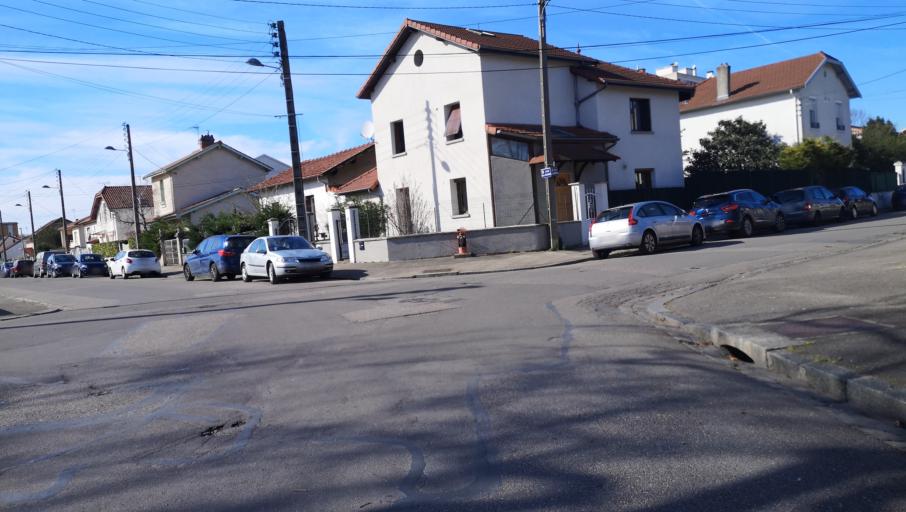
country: FR
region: Rhone-Alpes
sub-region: Departement du Rhone
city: Villeurbanne
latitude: 45.7755
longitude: 4.8964
